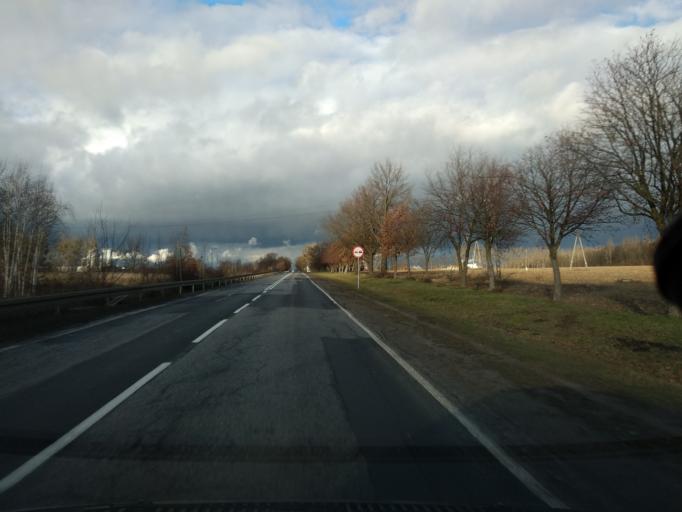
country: PL
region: Greater Poland Voivodeship
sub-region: Konin
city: Konin
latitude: 52.2581
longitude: 18.2685
